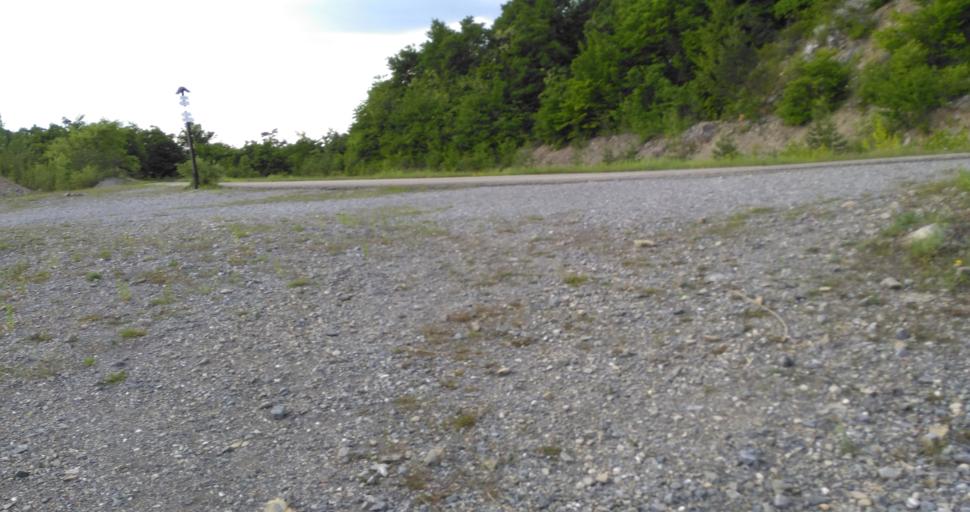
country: CZ
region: South Moravian
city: Bilovice nad Svitavou
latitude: 49.2207
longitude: 16.6681
